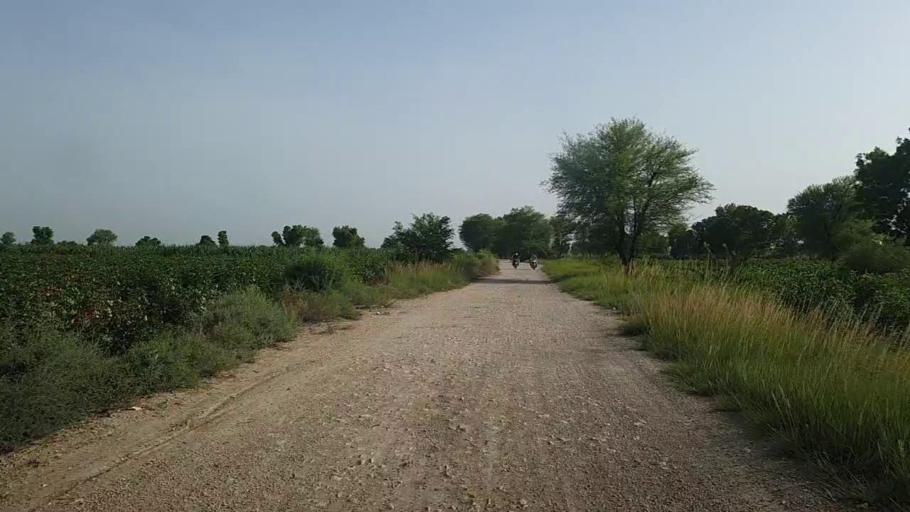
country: PK
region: Sindh
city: Pad Idan
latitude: 26.7561
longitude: 68.2572
